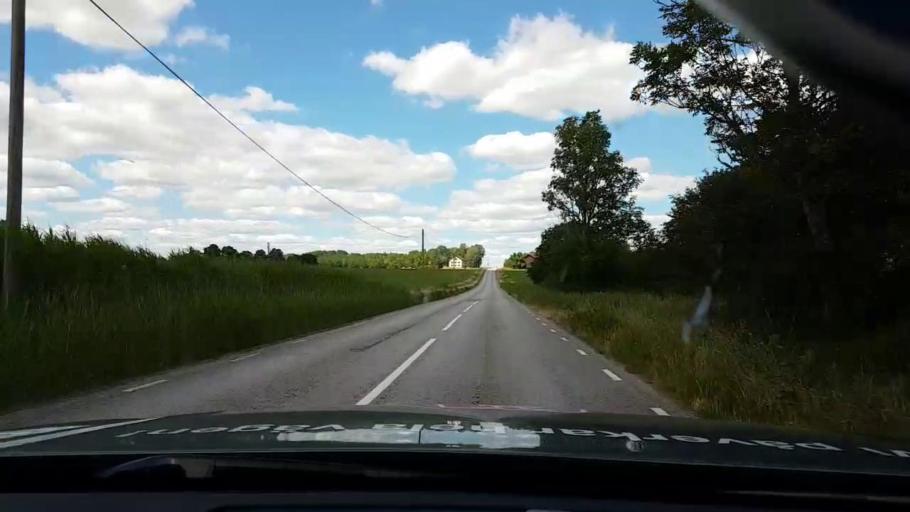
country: SE
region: Kalmar
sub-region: Vasterviks Kommun
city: Forserum
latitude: 58.0429
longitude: 16.4210
